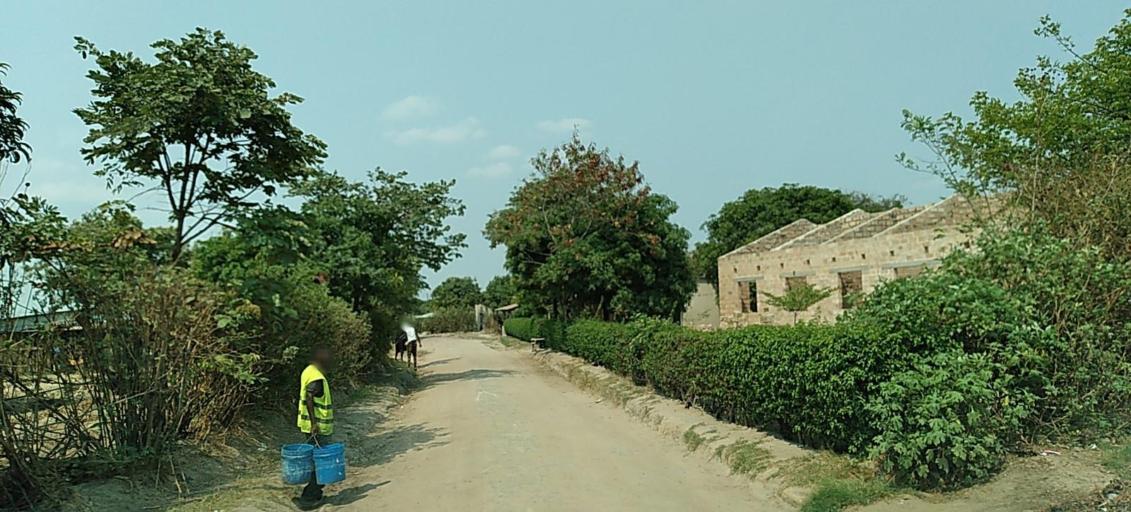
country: ZM
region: Copperbelt
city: Chambishi
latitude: -12.6297
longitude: 28.0751
